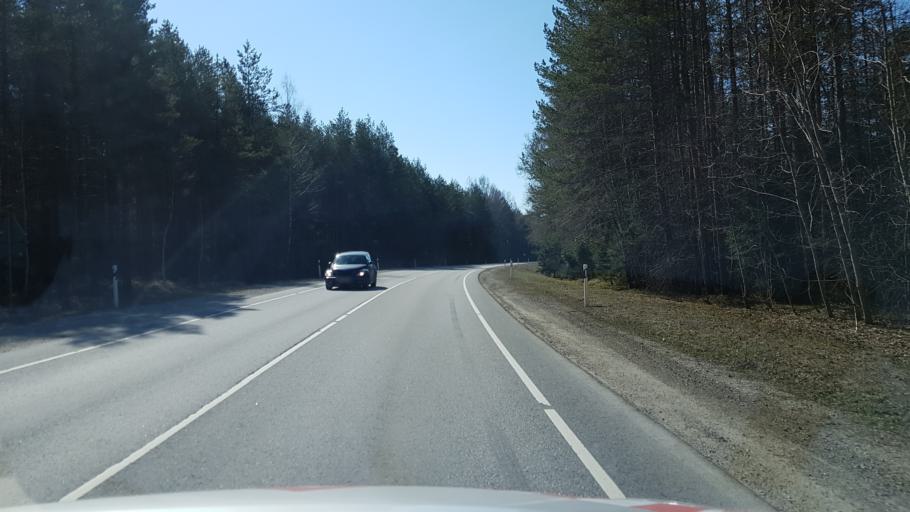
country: EE
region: Ida-Virumaa
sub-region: Kohtla-Jaerve linn
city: Kohtla-Jarve
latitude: 59.3337
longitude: 27.2647
